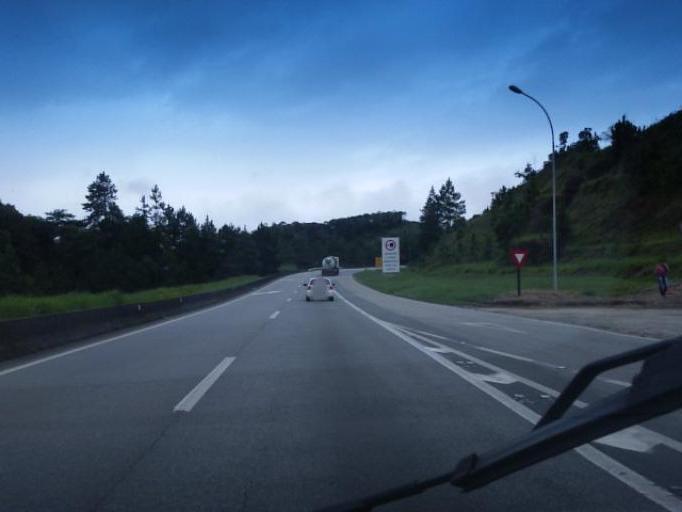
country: BR
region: Parana
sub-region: Campina Grande Do Sul
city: Campina Grande do Sul
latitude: -25.1082
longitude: -48.8356
